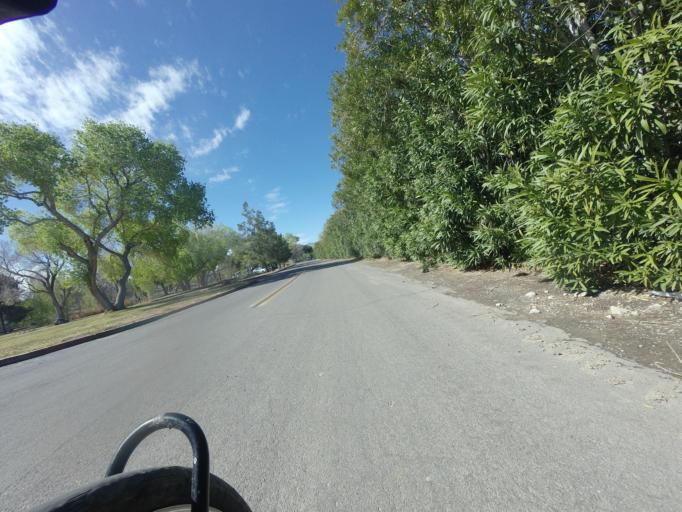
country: US
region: Nevada
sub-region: Clark County
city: North Las Vegas
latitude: 36.3258
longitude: -115.2660
